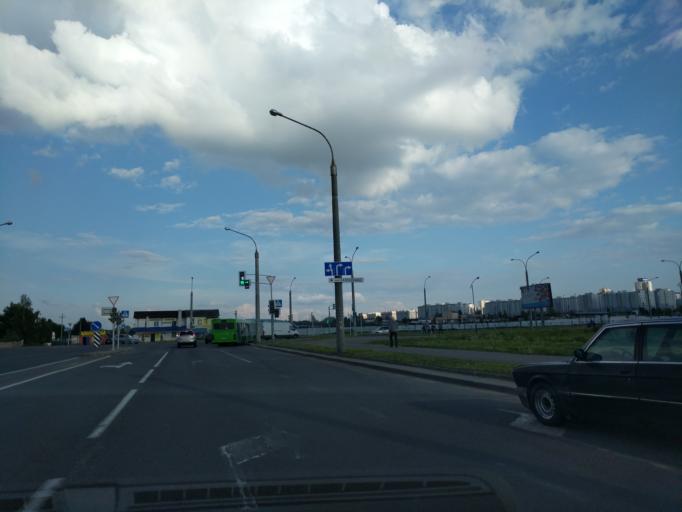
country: BY
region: Minsk
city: Zhdanovichy
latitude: 53.9314
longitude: 27.4446
